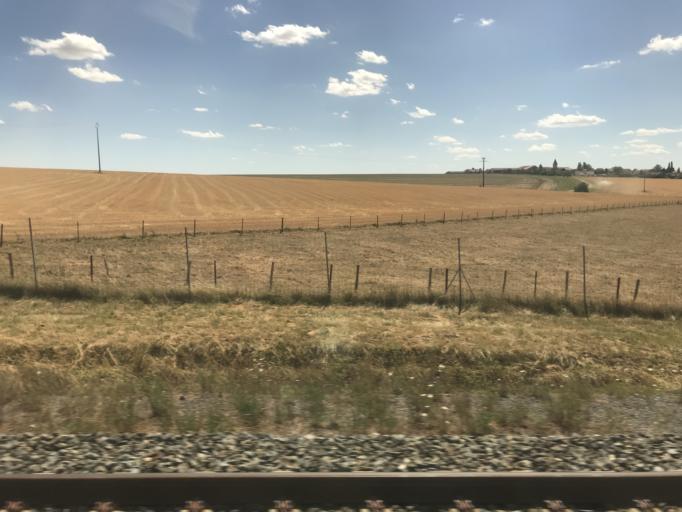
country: FR
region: Lorraine
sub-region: Departement de la Moselle
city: Verny
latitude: 48.9587
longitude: 6.2364
